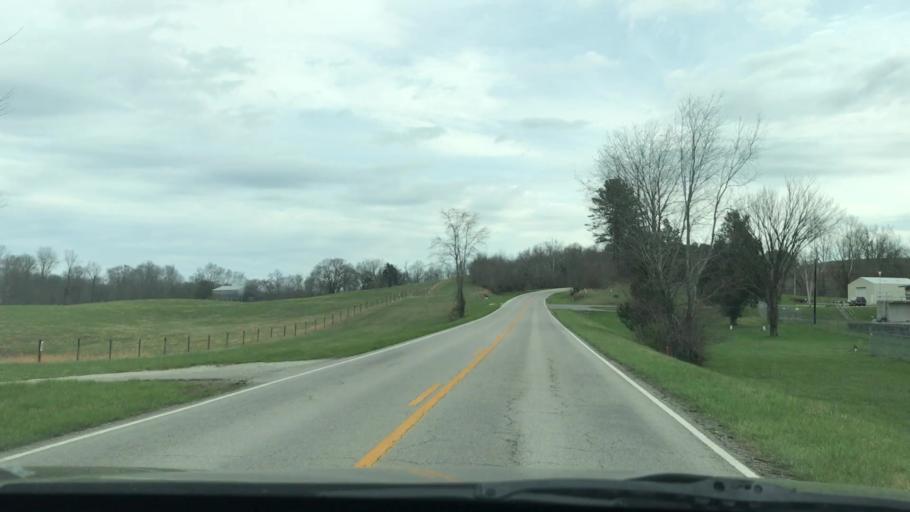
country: US
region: Kentucky
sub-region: Hart County
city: Munfordville
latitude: 37.3166
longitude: -85.7628
